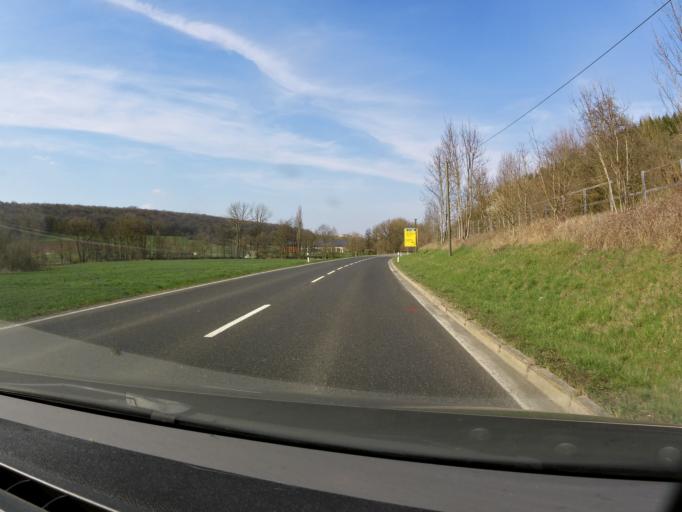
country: DE
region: Baden-Wuerttemberg
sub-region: Regierungsbezirk Stuttgart
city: Creglingen
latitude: 49.4809
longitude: 10.0201
